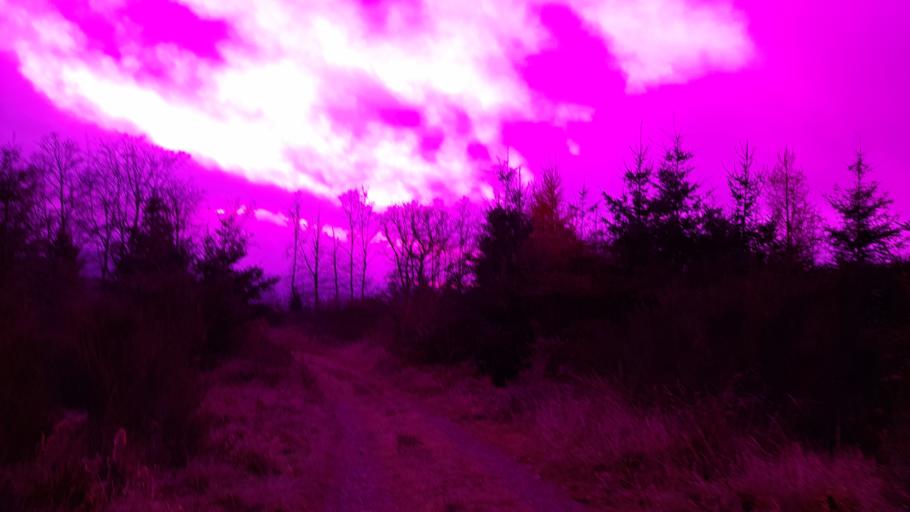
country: DE
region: Rheinland-Pfalz
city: Dasburg
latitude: 50.0646
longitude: 6.1082
